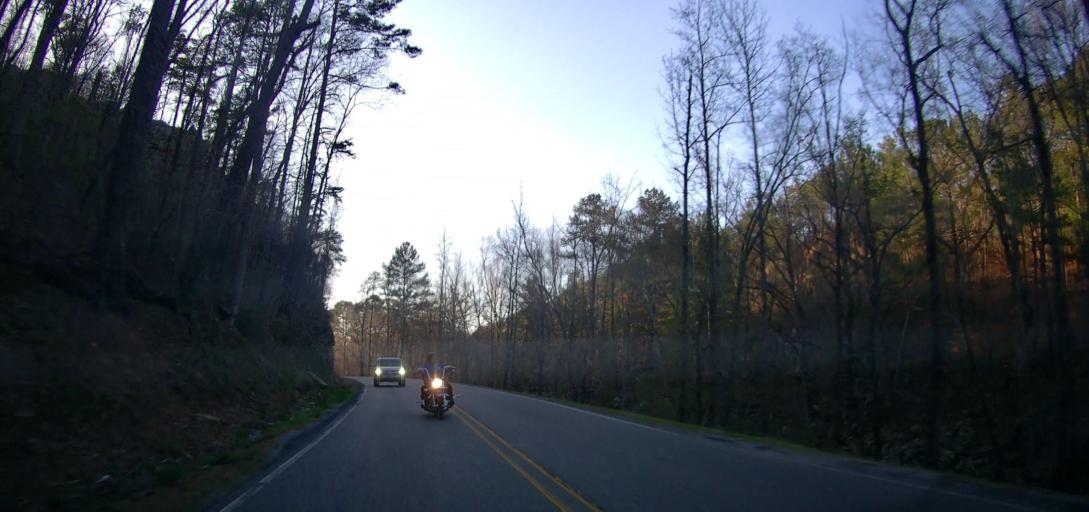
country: US
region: Alabama
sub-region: Shelby County
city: Chelsea
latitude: 33.3488
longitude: -86.6431
